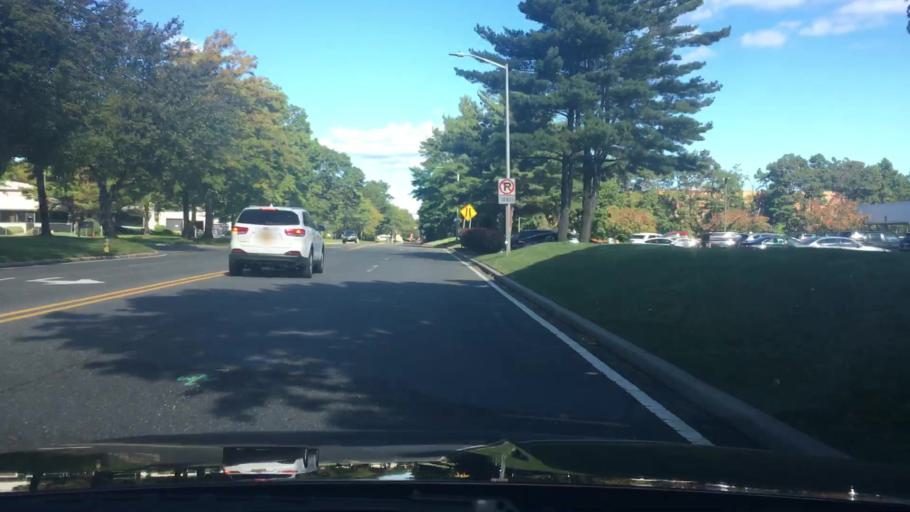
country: US
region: New York
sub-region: Suffolk County
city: Brentwood
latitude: 40.8072
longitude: -73.2556
